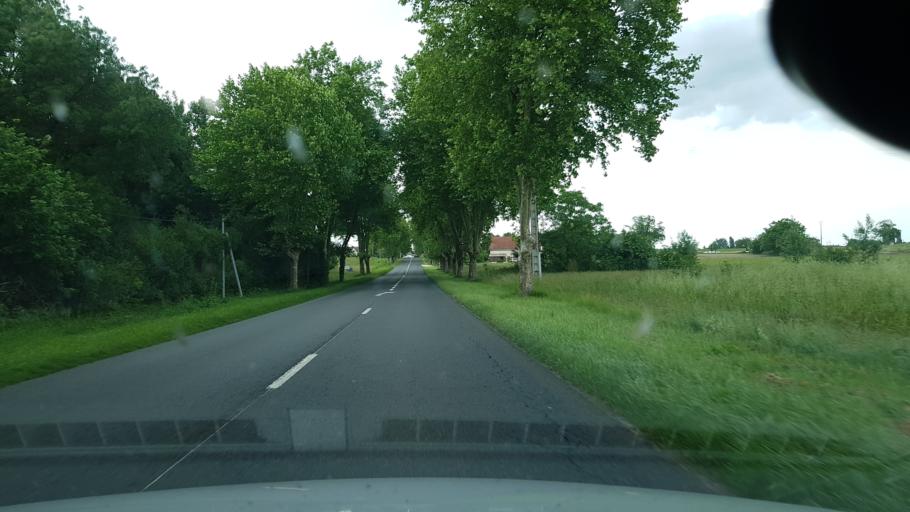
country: FR
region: Centre
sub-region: Departement du Loir-et-Cher
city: Chatillon-sur-Cher
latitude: 47.3369
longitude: 1.4842
